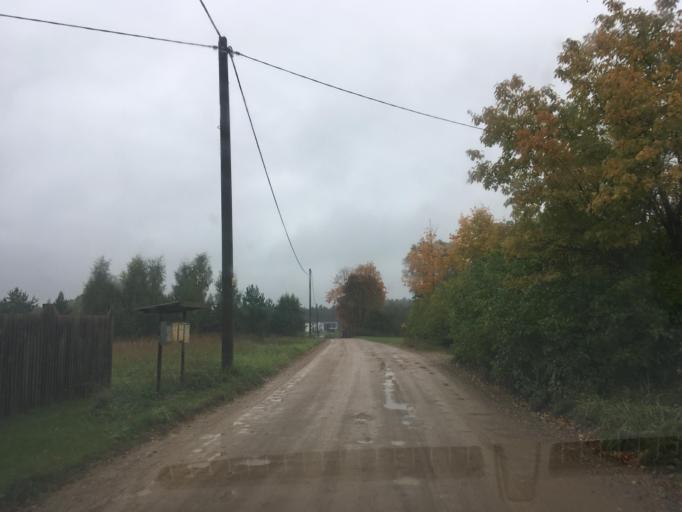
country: EE
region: Tartu
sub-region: UElenurme vald
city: Ulenurme
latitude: 58.3413
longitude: 26.7951
